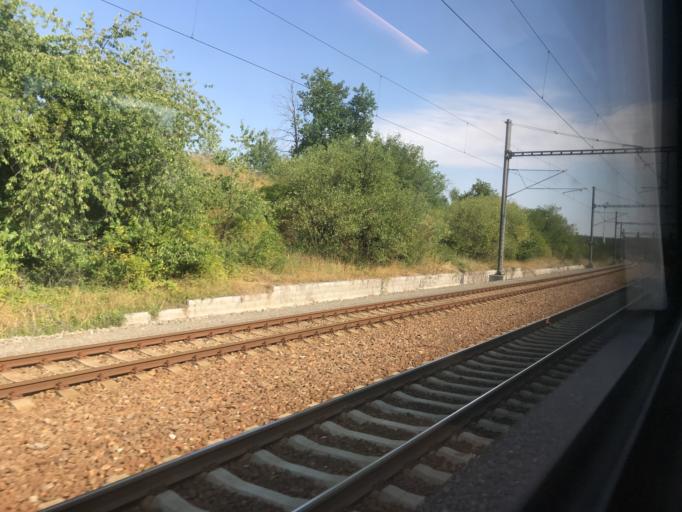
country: CZ
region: Central Bohemia
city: Votice
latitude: 49.6707
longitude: 14.6259
